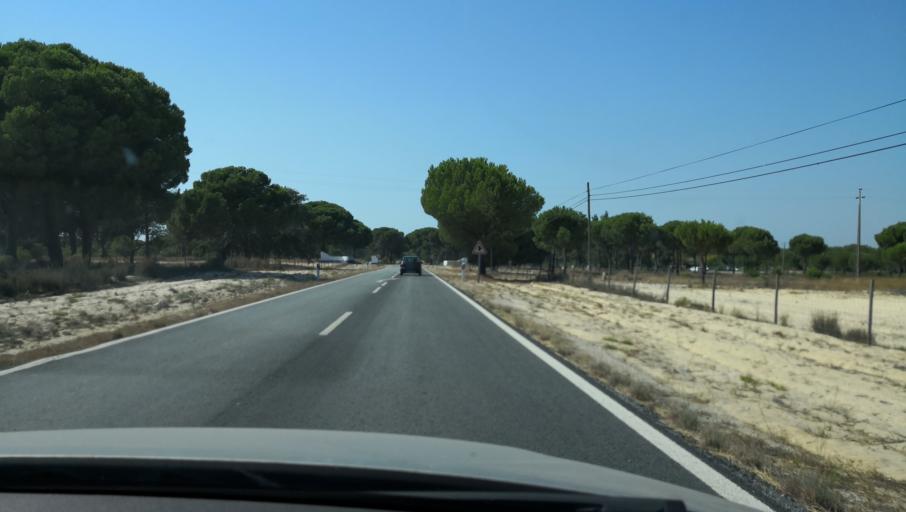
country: PT
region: Setubal
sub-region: Alcacer do Sal
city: Alcacer do Sal
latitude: 38.3940
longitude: -8.6556
